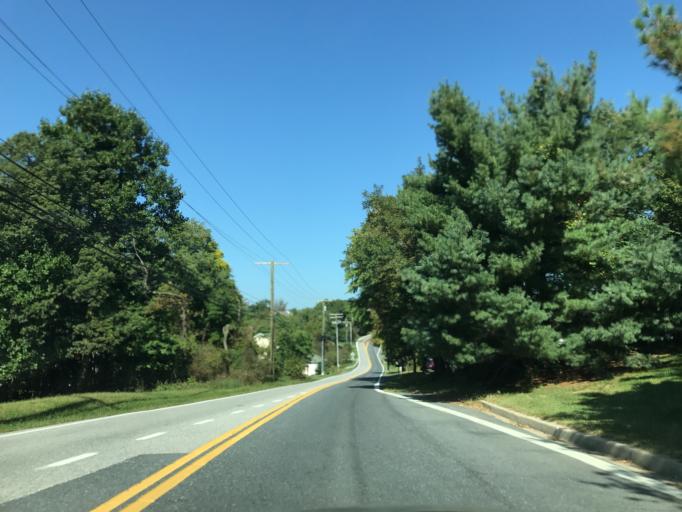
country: US
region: Maryland
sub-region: Anne Arundel County
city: Jessup
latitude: 39.1961
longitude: -76.7795
